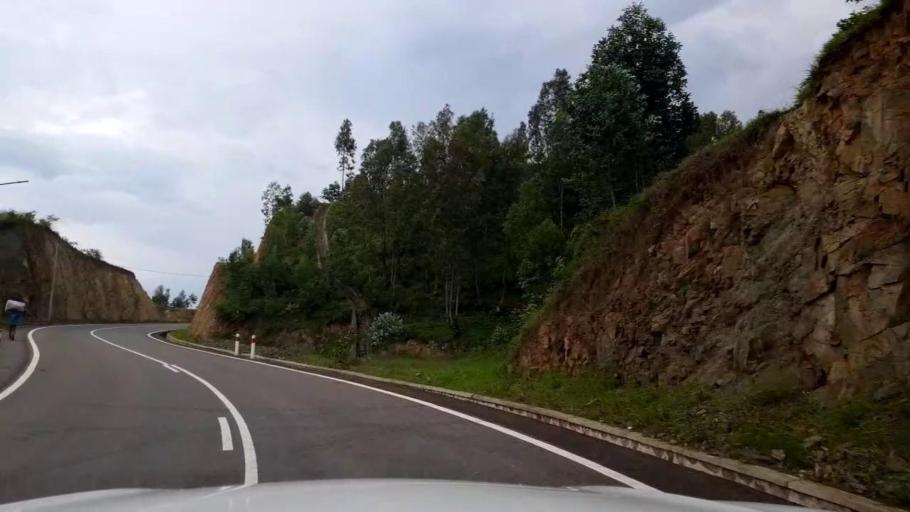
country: RW
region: Western Province
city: Kibuye
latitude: -2.0268
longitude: 29.3939
